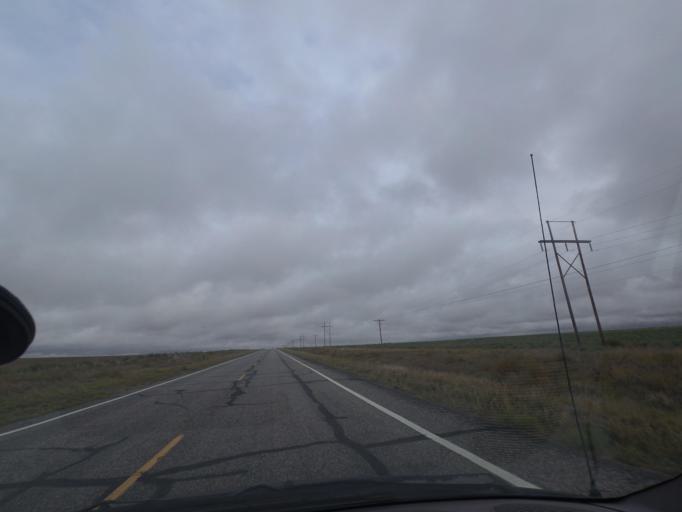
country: US
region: Colorado
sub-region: Washington County
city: Akron
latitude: 39.7402
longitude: -103.2993
